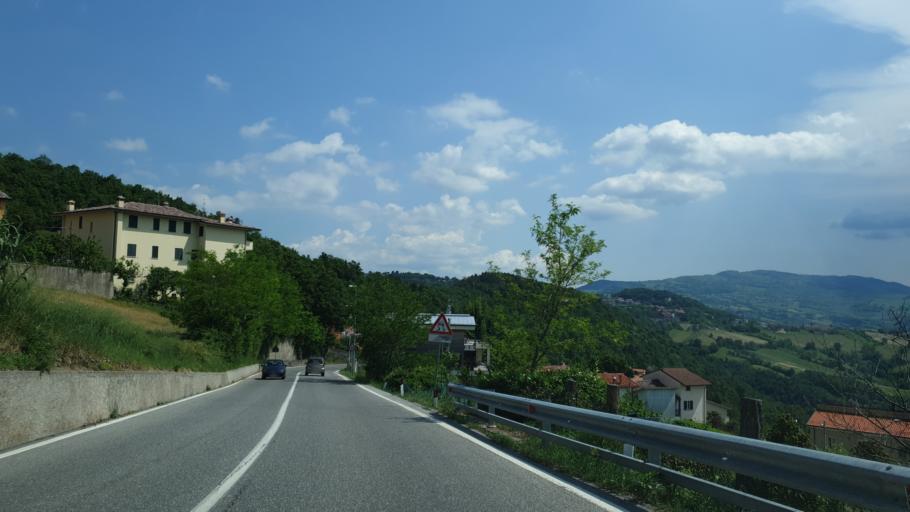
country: SM
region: San Marino
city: San Marino
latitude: 43.9356
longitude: 12.4372
